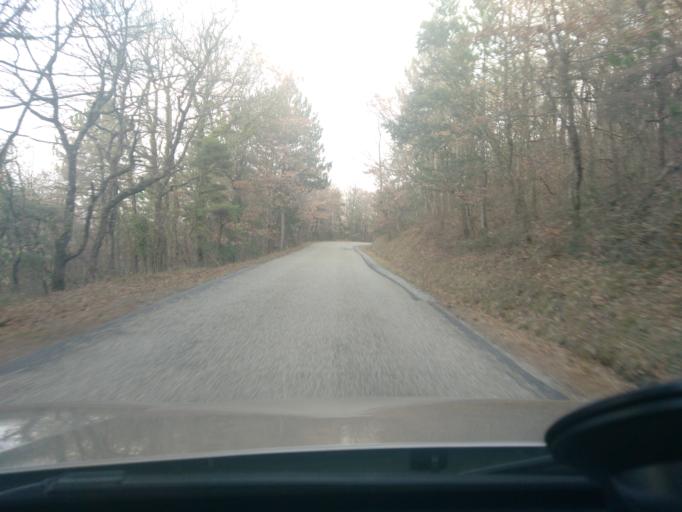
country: FR
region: Rhone-Alpes
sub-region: Departement de la Drome
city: Montboucher-sur-Jabron
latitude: 44.5143
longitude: 4.8621
